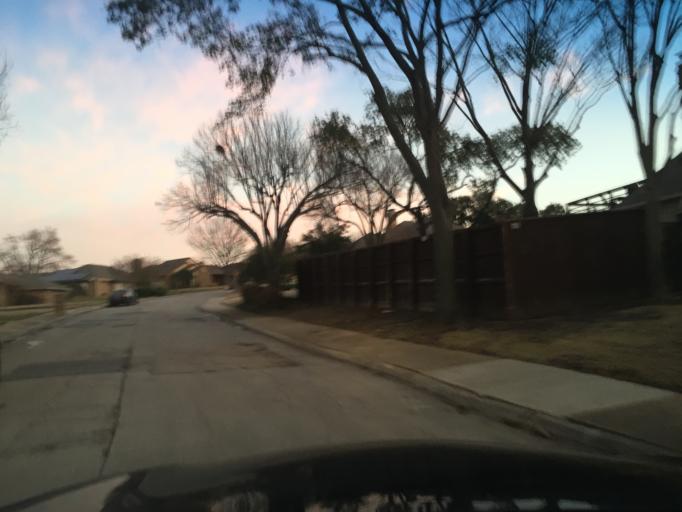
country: US
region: Texas
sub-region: Dallas County
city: Carrollton
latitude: 32.9911
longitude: -96.8960
